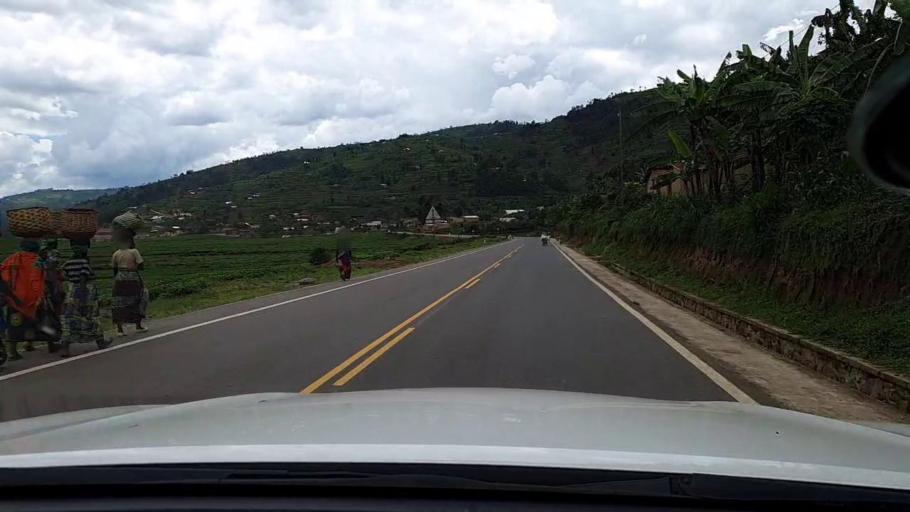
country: RW
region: Northern Province
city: Byumba
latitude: -1.6478
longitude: 29.9020
